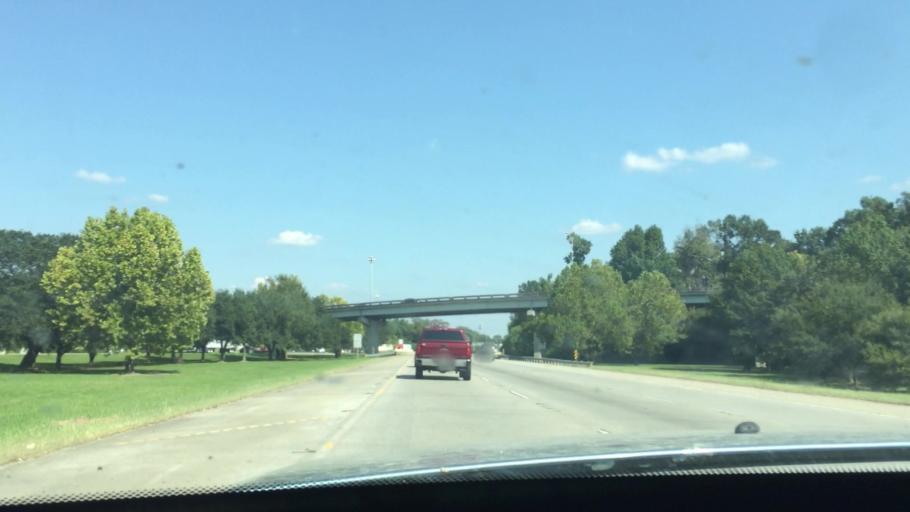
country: US
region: Louisiana
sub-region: East Baton Rouge Parish
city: Westminster
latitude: 30.4185
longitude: -91.1150
